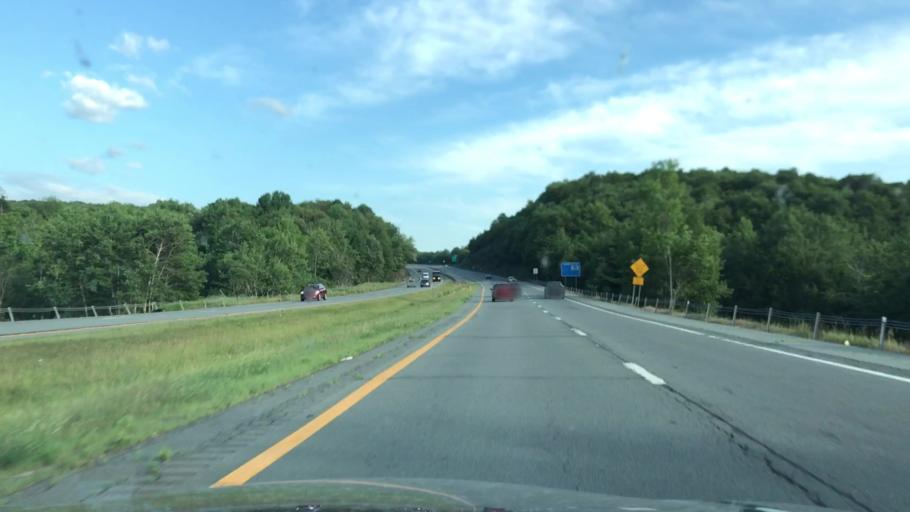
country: US
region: New York
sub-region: Sullivan County
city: Monticello
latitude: 41.6776
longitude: -74.7166
